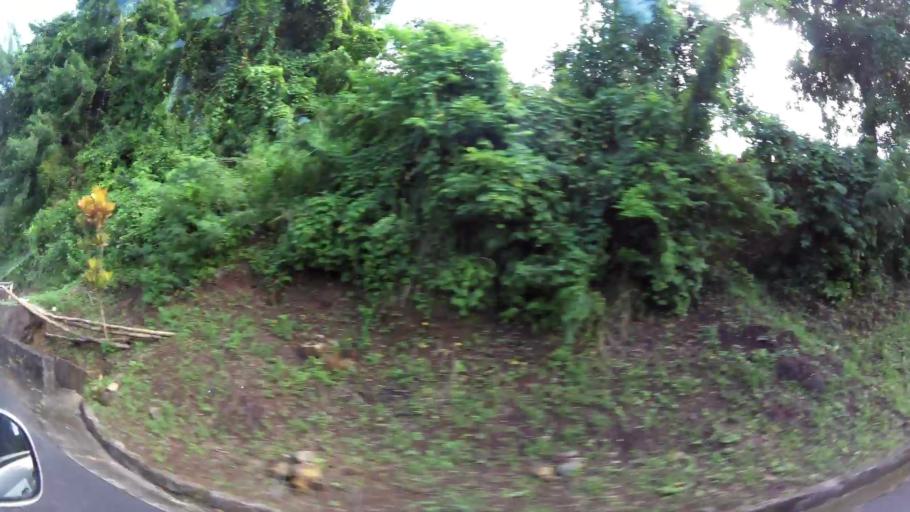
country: GD
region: Saint Mark
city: Victoria
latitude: 12.2155
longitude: -61.6893
